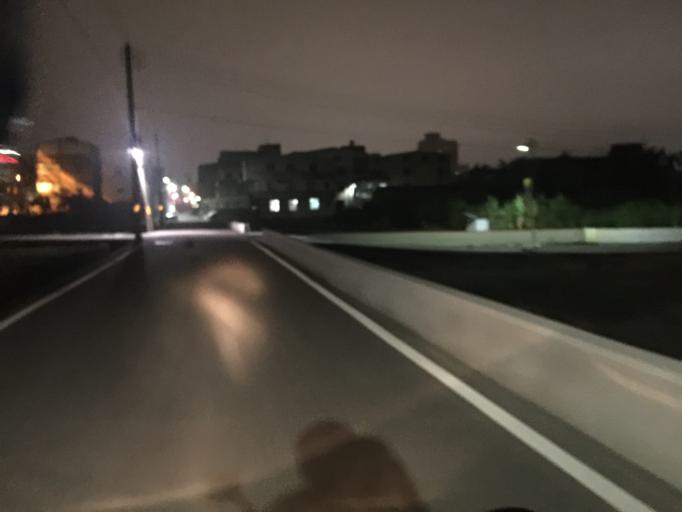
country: TW
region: Taiwan
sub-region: Miaoli
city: Miaoli
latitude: 24.5793
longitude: 120.8287
